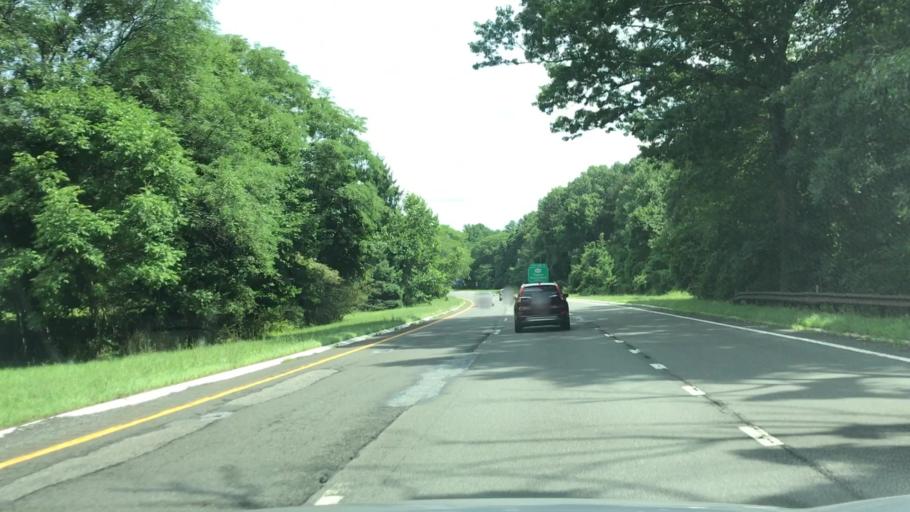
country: US
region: New York
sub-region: Rockland County
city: Orangeburg
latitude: 41.0425
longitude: -73.9568
